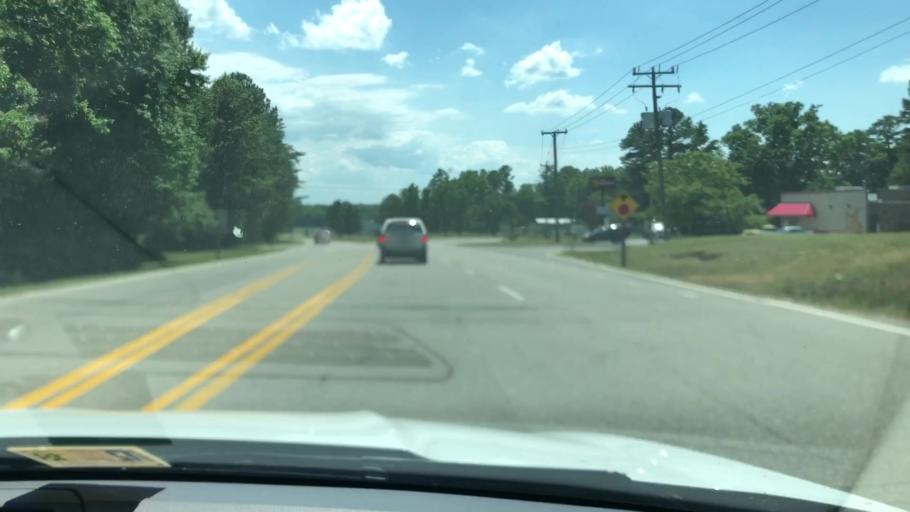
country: US
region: Virginia
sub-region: Middlesex County
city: Saluda
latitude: 37.5979
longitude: -76.6022
